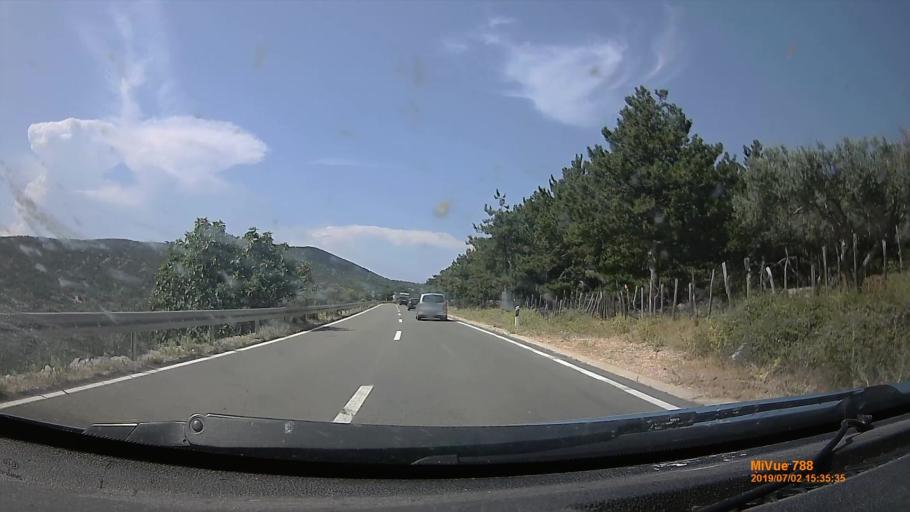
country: HR
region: Primorsko-Goranska
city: Cres
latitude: 44.9775
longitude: 14.4120
